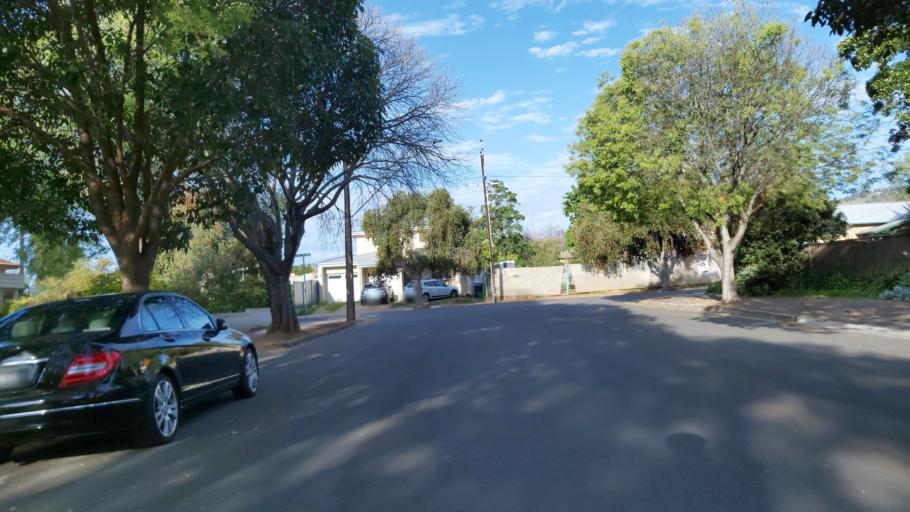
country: AU
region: South Australia
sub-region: Unley
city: Fullarton
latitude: -34.9525
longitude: 138.6313
